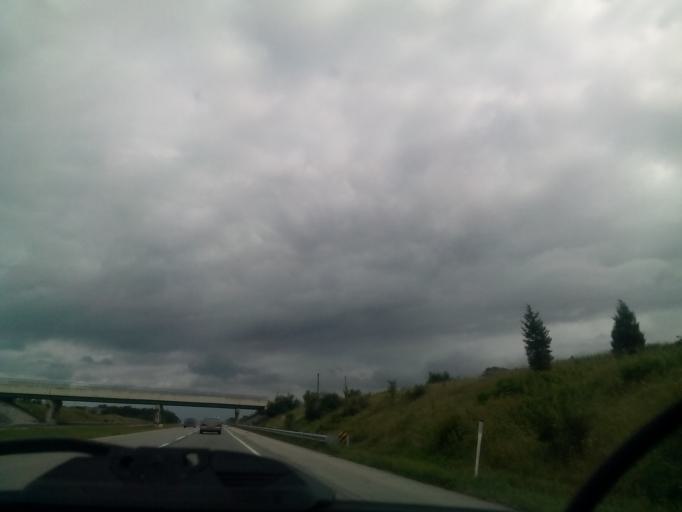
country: US
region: Indiana
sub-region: Steuben County
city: Fremont
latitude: 41.6819
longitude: -84.8796
